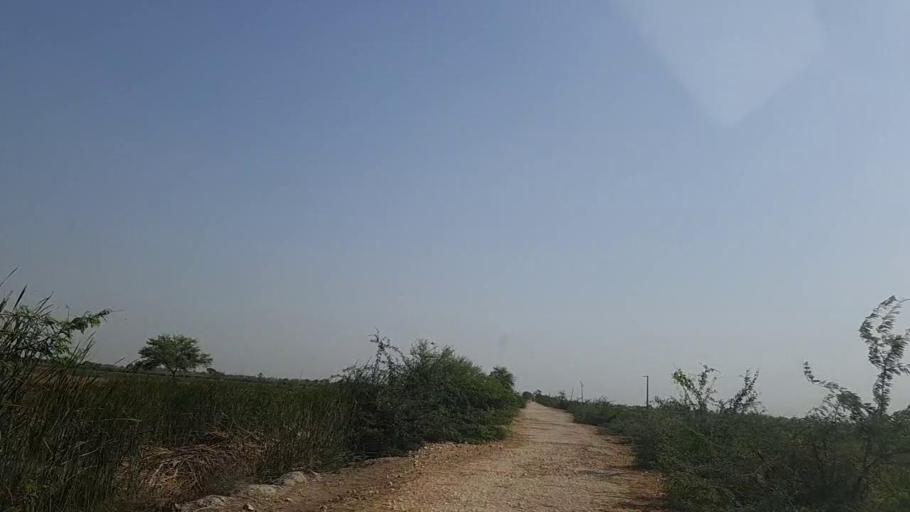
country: PK
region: Sindh
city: Daro Mehar
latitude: 24.7203
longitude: 68.0856
